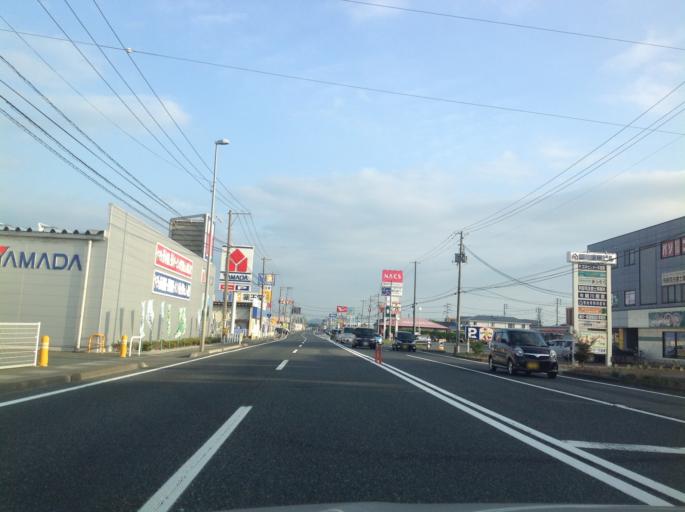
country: JP
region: Iwate
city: Morioka-shi
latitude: 39.5500
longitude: 141.1676
